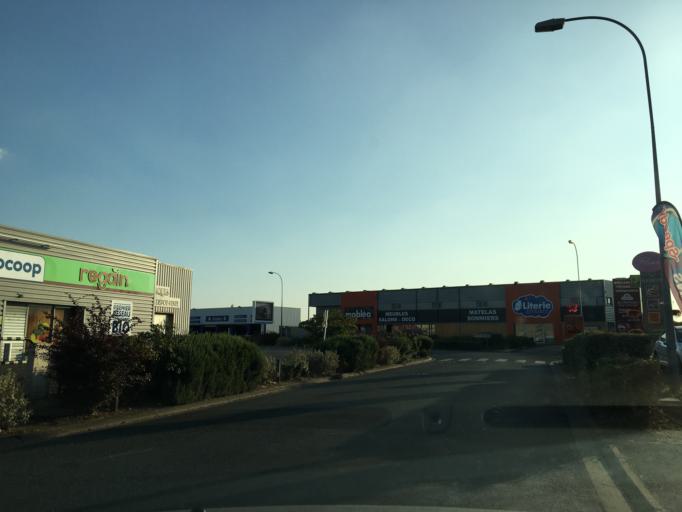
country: FR
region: Poitou-Charentes
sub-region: Departement de la Charente-Maritime
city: Angoulins
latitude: 46.1079
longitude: -1.1004
